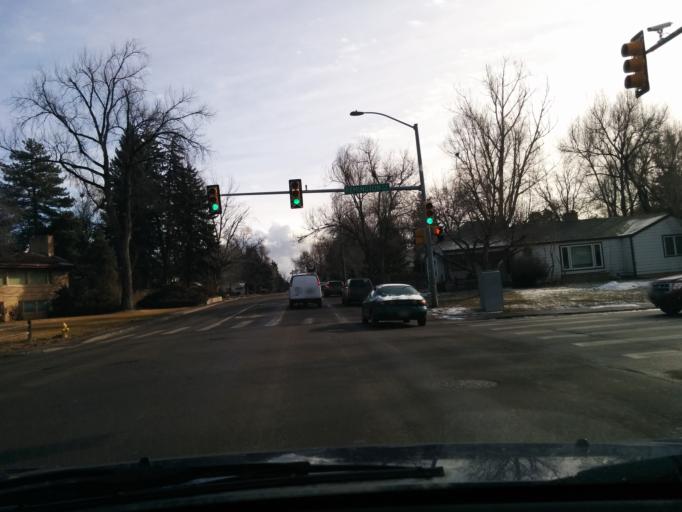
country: US
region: Colorado
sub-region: Larimer County
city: Fort Collins
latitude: 40.5671
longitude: -105.0757
